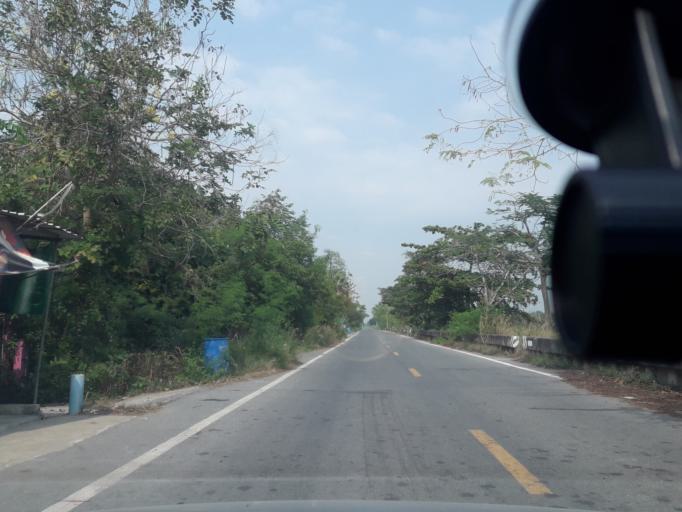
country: TH
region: Pathum Thani
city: Nong Suea
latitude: 14.1985
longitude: 100.8915
